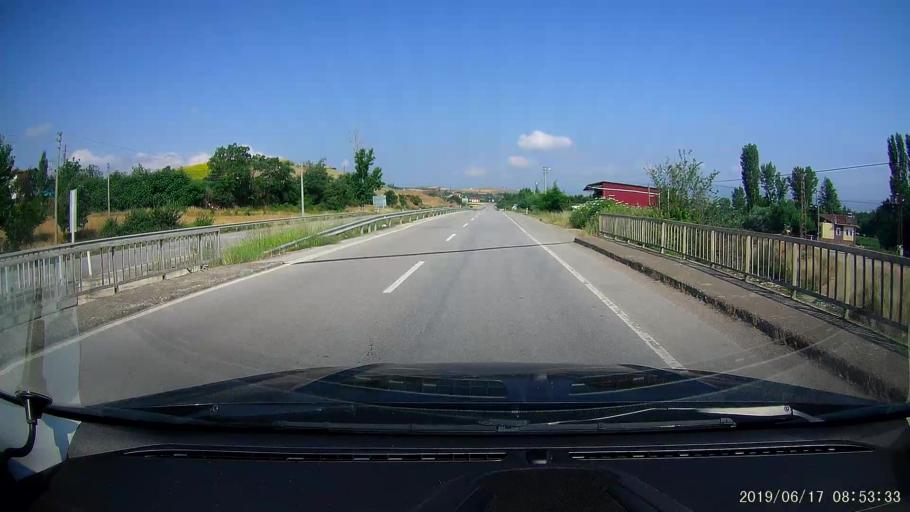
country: TR
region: Tokat
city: Erbaa
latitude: 40.7109
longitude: 36.4791
